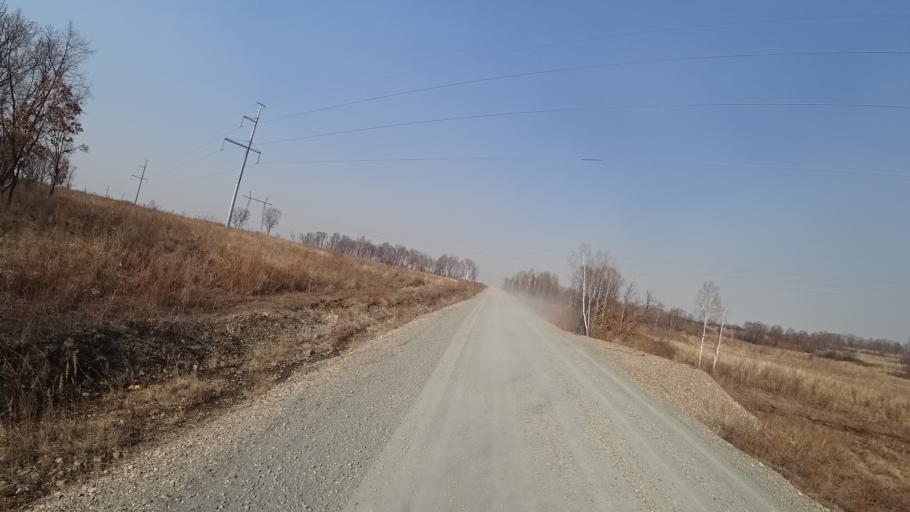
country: RU
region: Amur
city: Novobureyskiy
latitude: 49.8020
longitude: 129.9609
